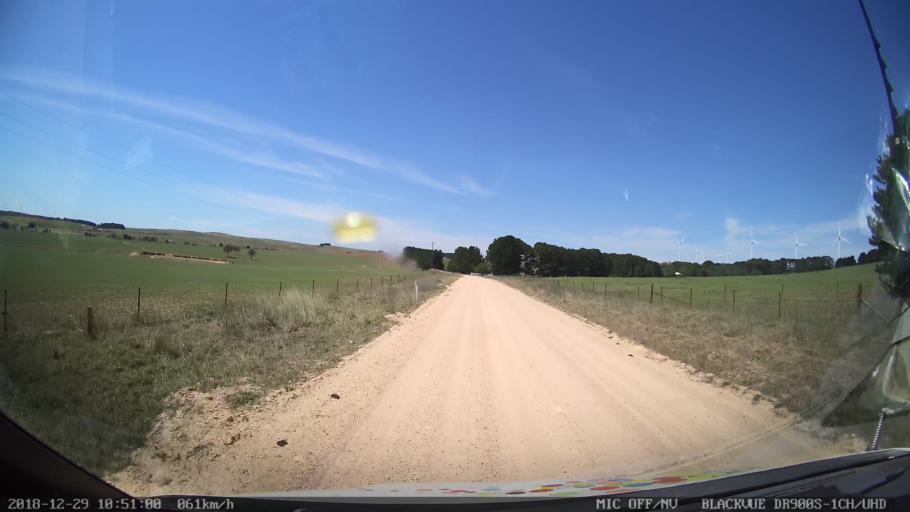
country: AU
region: New South Wales
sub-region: Palerang
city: Bungendore
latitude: -35.0859
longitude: 149.5239
